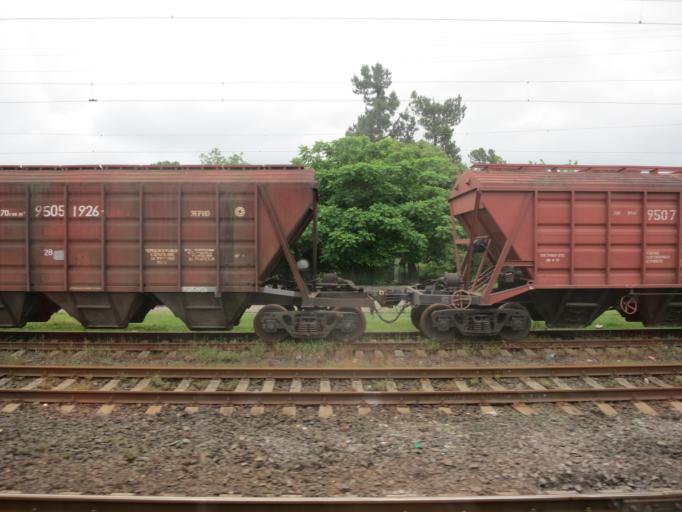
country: GE
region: Ajaria
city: Kobuleti
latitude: 41.8107
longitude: 41.7813
